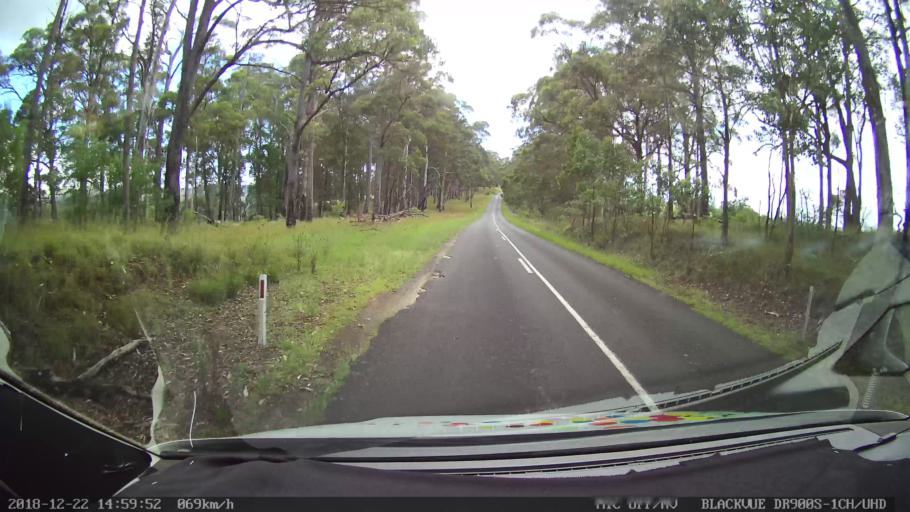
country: AU
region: New South Wales
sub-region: Bellingen
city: Dorrigo
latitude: -30.2493
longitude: 152.4775
